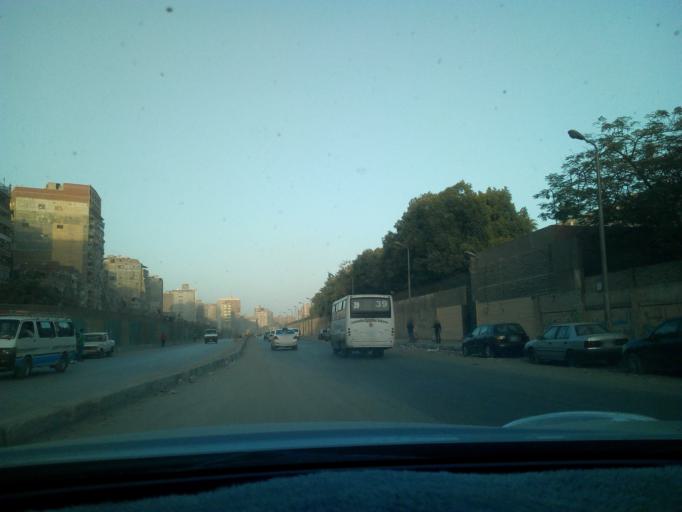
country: EG
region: Muhafazat al Qalyubiyah
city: Al Khankah
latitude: 30.1239
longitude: 31.3466
